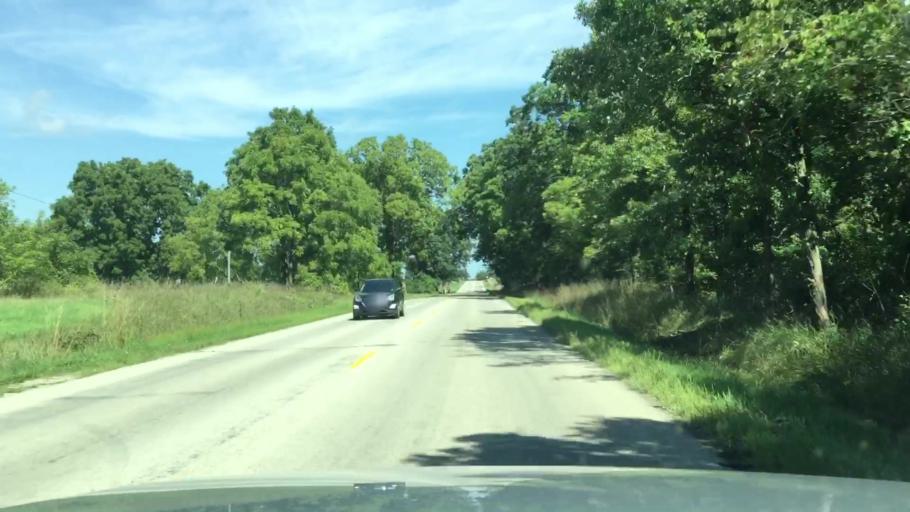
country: US
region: Michigan
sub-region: Lenawee County
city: Manitou Beach-Devils Lake
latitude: 42.0391
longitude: -84.2763
